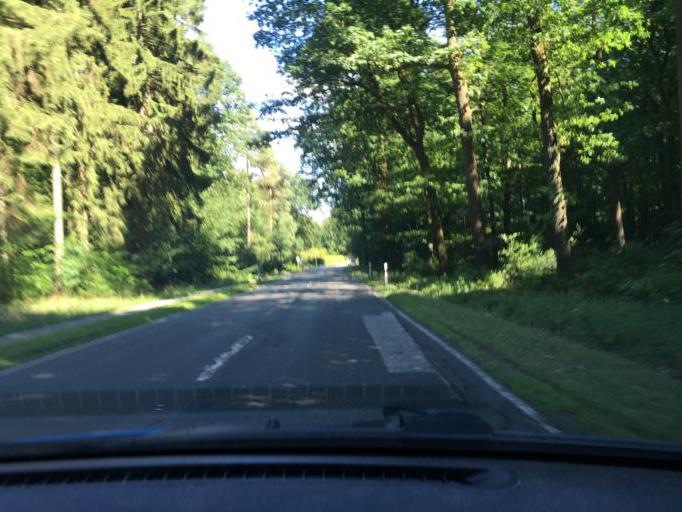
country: DE
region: Lower Saxony
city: Bendestorf
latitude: 53.3429
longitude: 9.9557
